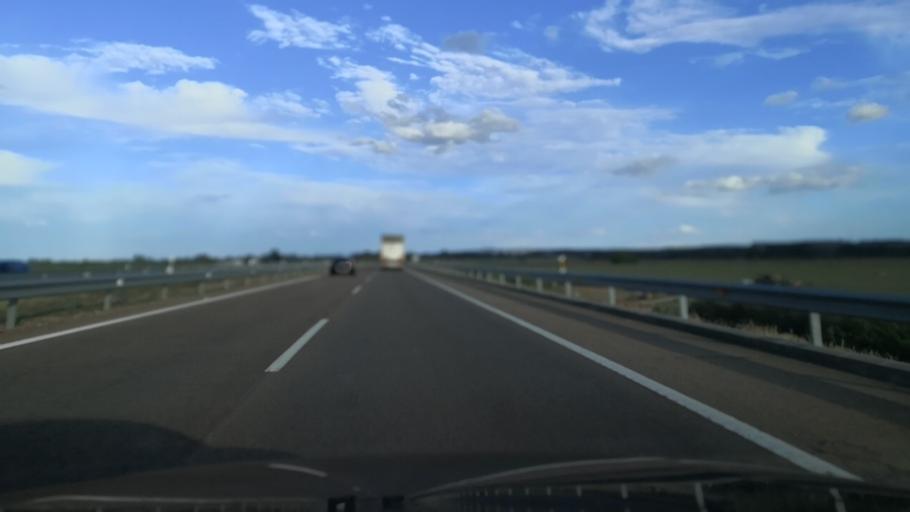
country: ES
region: Extremadura
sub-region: Provincia de Badajoz
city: Badajoz
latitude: 38.9087
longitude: -6.9415
